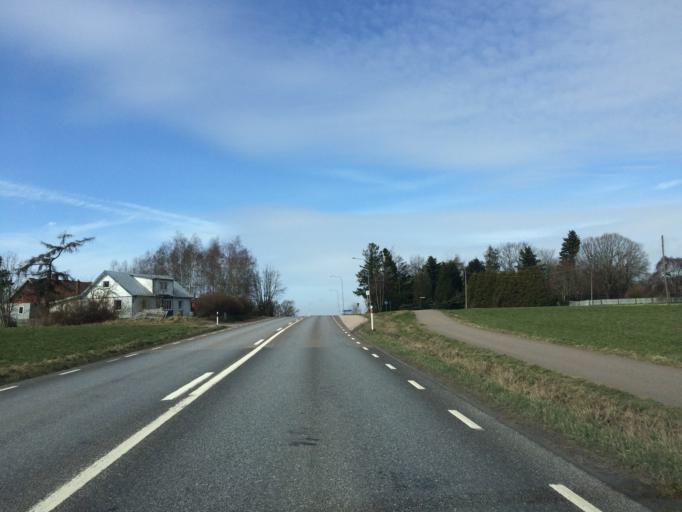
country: SE
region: Halland
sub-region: Laholms Kommun
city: Veinge
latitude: 56.5577
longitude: 13.0363
